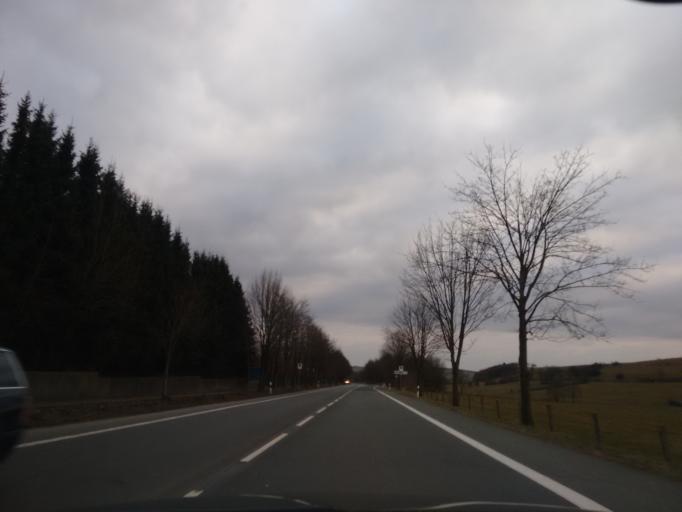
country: DE
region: North Rhine-Westphalia
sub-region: Regierungsbezirk Detmold
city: Altenbeken
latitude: 51.7318
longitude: 8.9465
